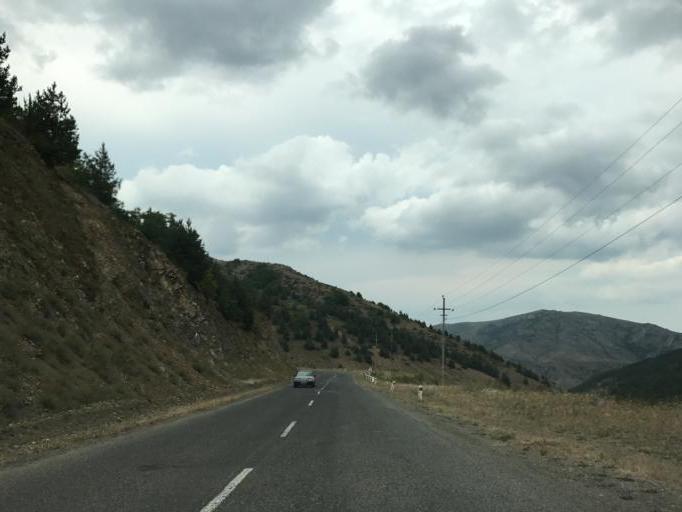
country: AZ
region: Susa
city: Shushi
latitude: 39.7007
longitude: 46.6518
